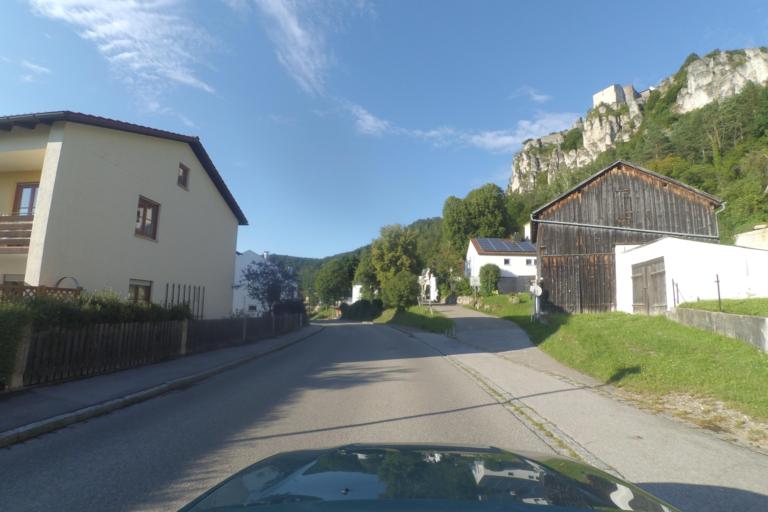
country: DE
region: Bavaria
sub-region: Upper Bavaria
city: Bohmfeld
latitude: 48.9264
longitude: 11.3764
